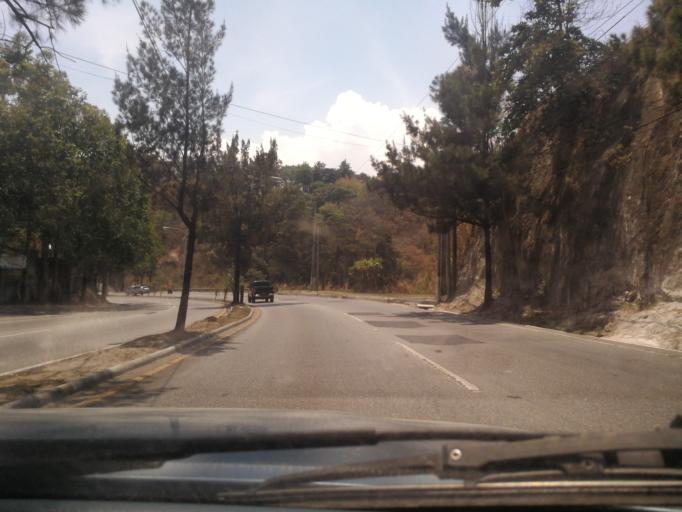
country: GT
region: Guatemala
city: Guatemala City
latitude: 14.6200
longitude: -90.4954
